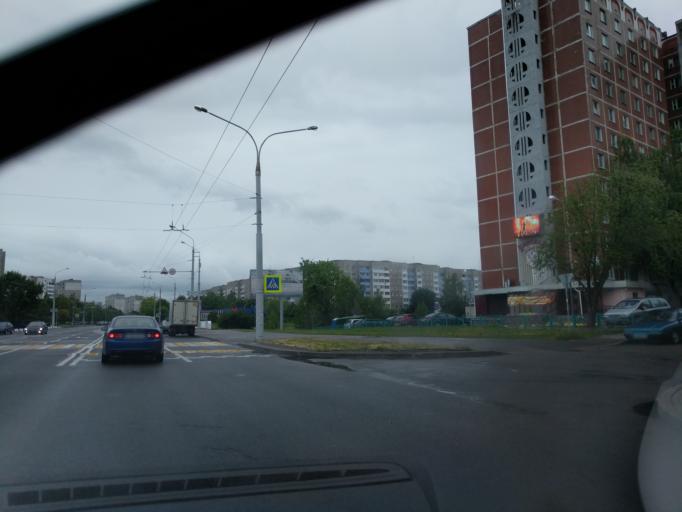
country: BY
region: Minsk
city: Novoye Medvezhino
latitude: 53.8584
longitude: 27.4725
